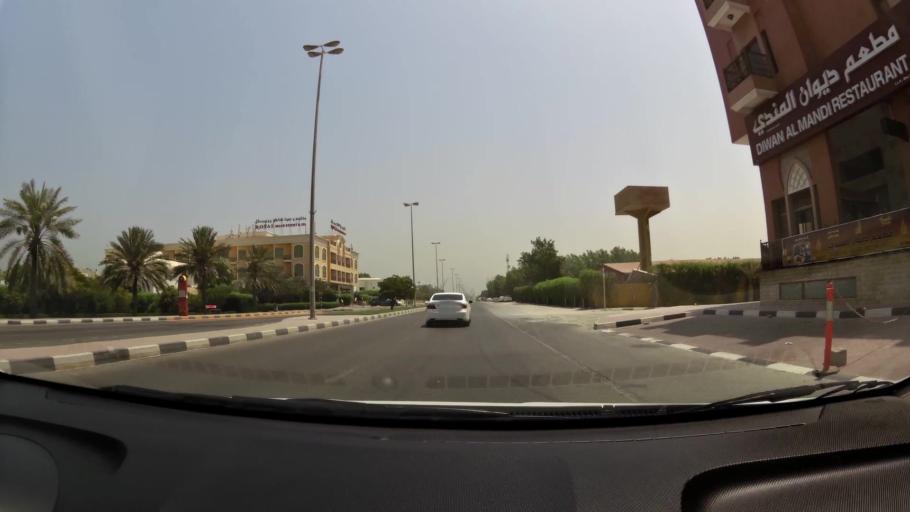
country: AE
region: Ash Shariqah
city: Sharjah
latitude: 25.3472
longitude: 55.3685
